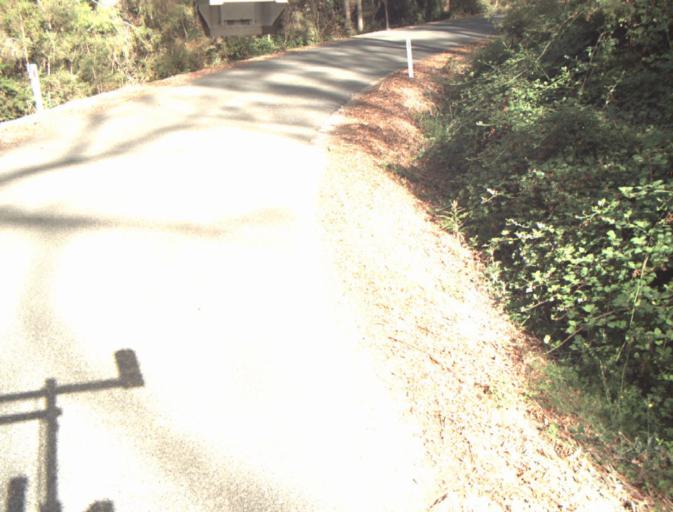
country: AU
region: Tasmania
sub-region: Launceston
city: Mayfield
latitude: -41.2691
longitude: 147.1620
